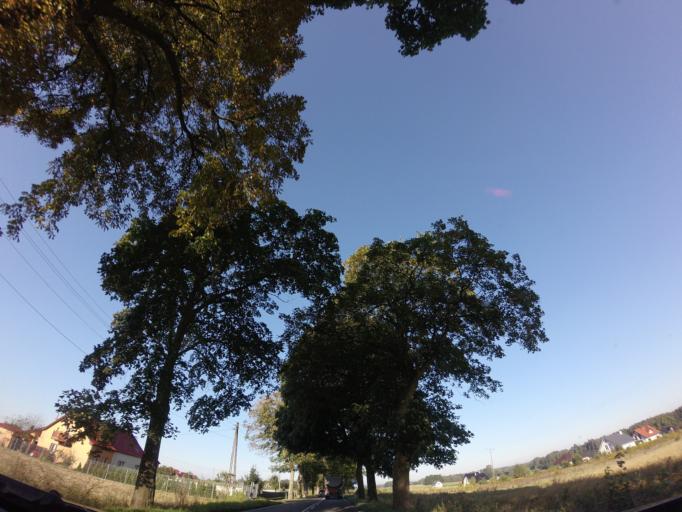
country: PL
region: West Pomeranian Voivodeship
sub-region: Powiat goleniowski
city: Mosty
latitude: 53.5523
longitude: 14.9003
